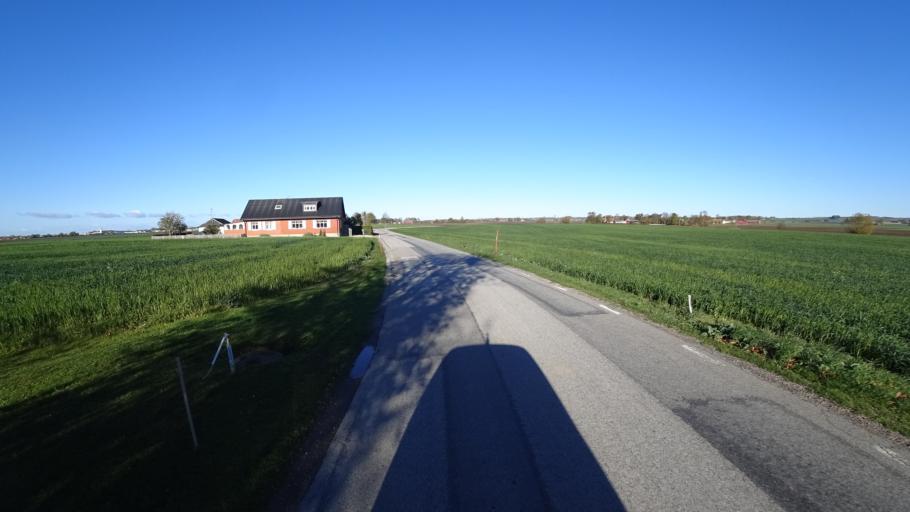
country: SE
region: Skane
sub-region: Staffanstorps Kommun
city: Staffanstorp
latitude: 55.6524
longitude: 13.2620
